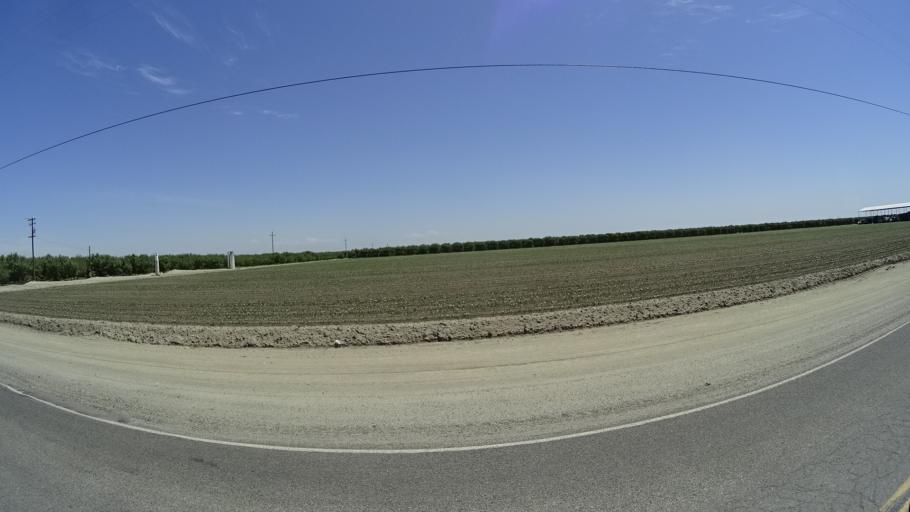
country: US
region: California
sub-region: Kings County
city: Corcoran
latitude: 36.1155
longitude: -119.6257
